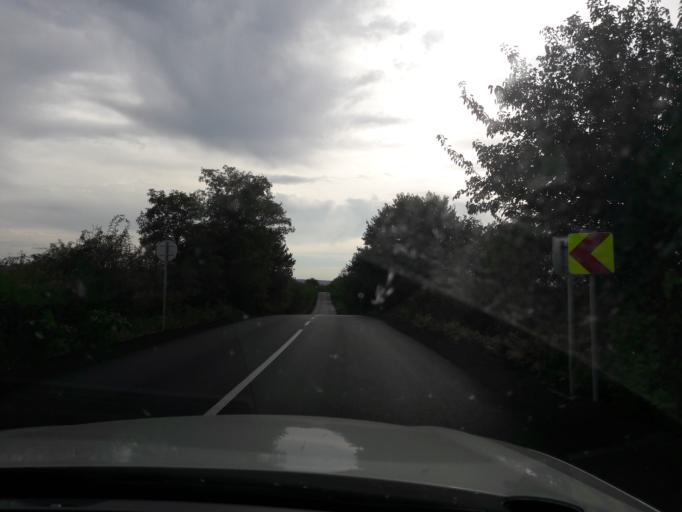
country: SK
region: Nitriansky
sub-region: Okres Nitra
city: Vrable
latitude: 48.1536
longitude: 18.4275
